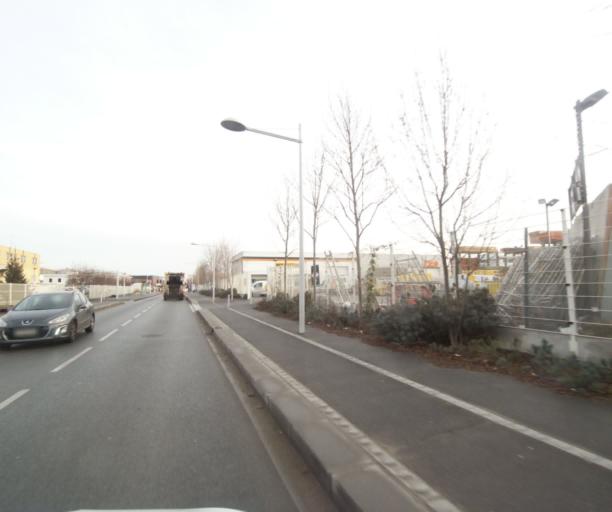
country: FR
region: Ile-de-France
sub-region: Departement des Yvelines
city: Carrieres-sur-Seine
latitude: 48.8940
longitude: 2.1818
